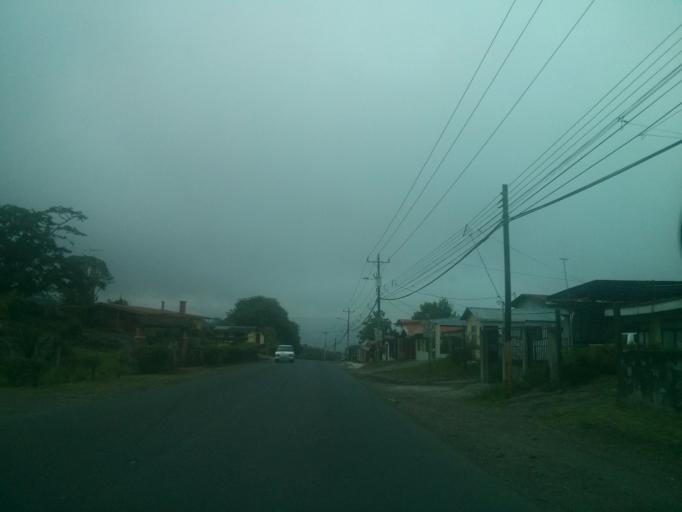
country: CR
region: Cartago
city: Cot
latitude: 9.8820
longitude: -83.8139
